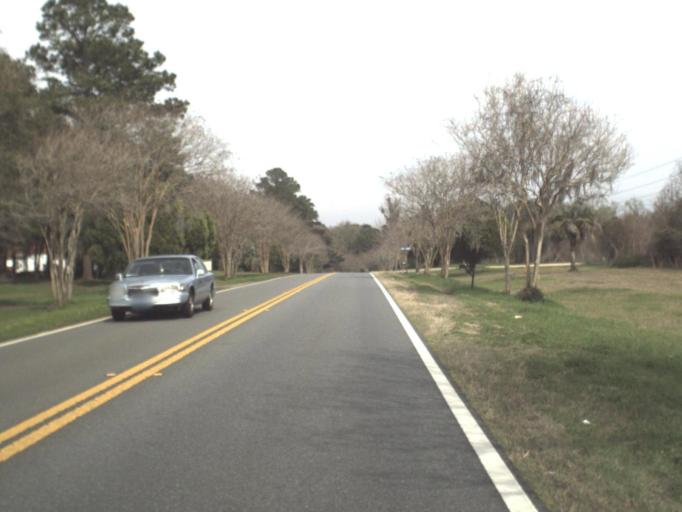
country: US
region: Florida
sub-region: Jefferson County
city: Monticello
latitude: 30.5280
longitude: -83.9982
